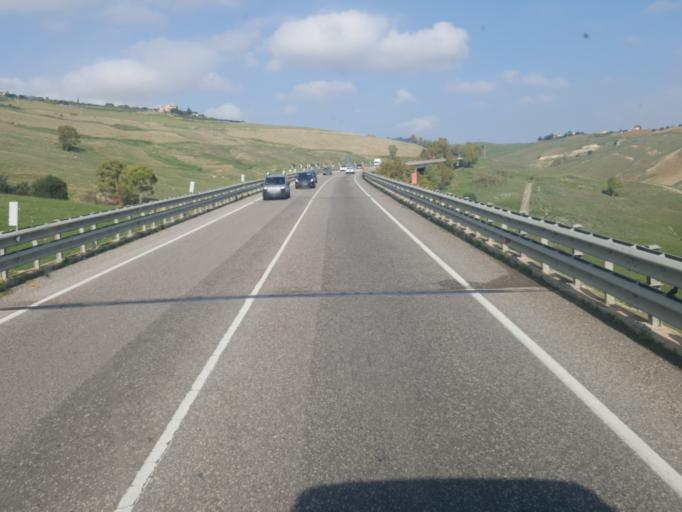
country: IT
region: Sicily
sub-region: Provincia di Caltanissetta
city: Caltanissetta
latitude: 37.4636
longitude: 14.1011
